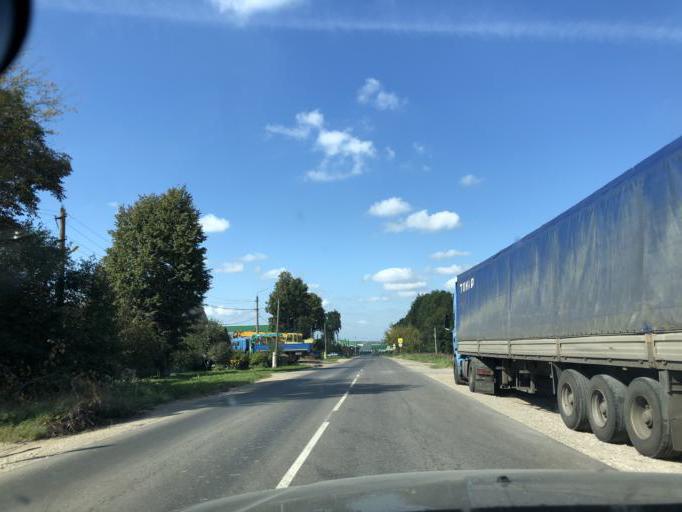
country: RU
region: Tula
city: Yasnogorsk
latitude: 54.4880
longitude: 37.6950
